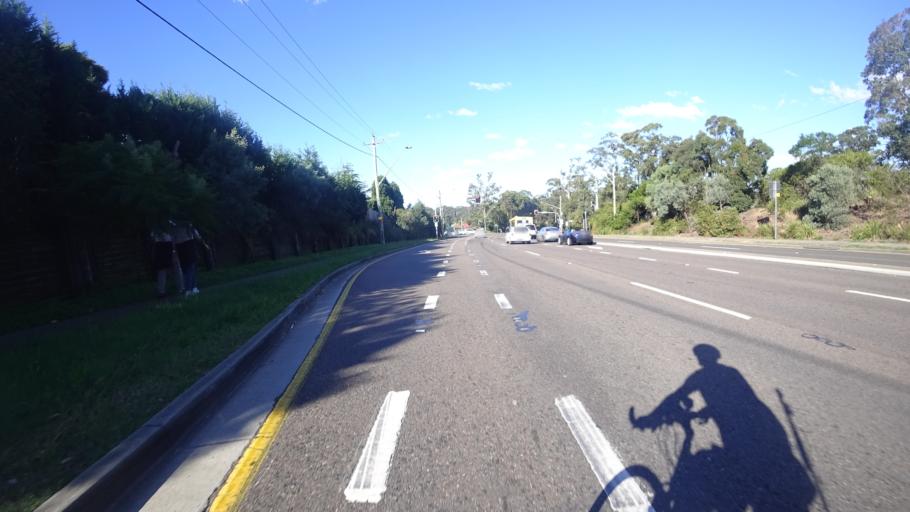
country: AU
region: New South Wales
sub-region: The Hills Shire
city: West Pennant
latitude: -33.7324
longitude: 151.0261
